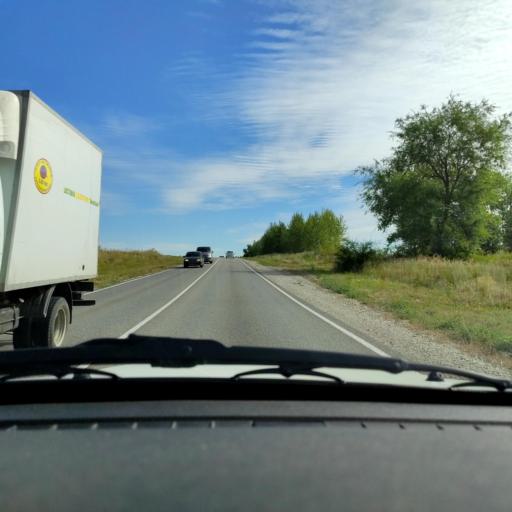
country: RU
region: Voronezj
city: Volya
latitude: 51.7185
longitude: 39.5406
